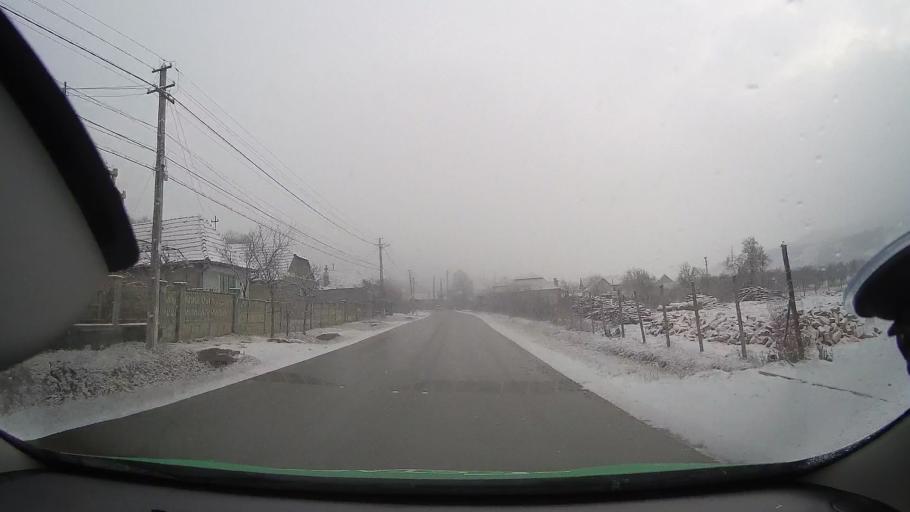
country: RO
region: Alba
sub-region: Municipiul Aiud
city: Ciumbrud
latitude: 46.3113
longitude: 23.7886
